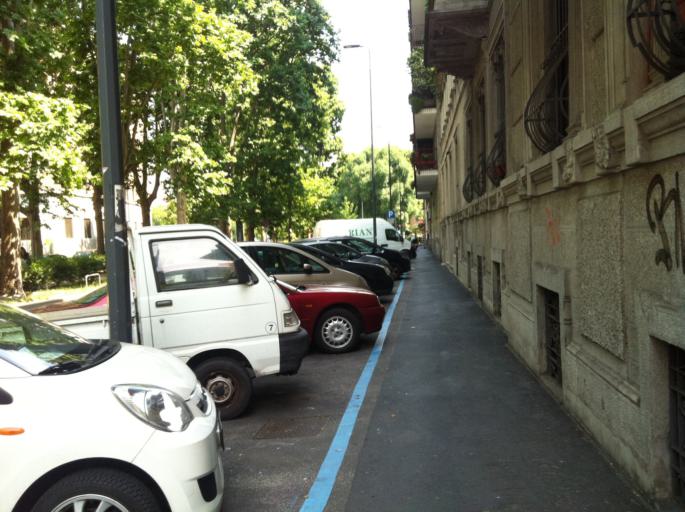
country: IT
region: Lombardy
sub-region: Citta metropolitana di Milano
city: Milano
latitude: 45.4716
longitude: 9.2176
